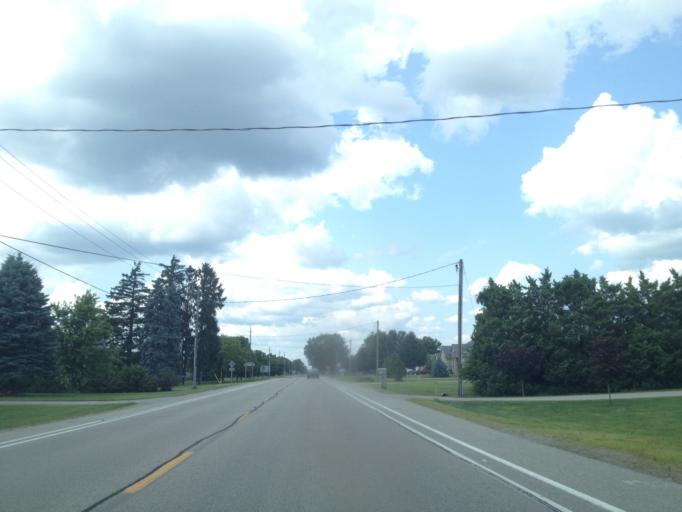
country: CA
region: Ontario
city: Aylmer
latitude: 42.6774
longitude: -80.9854
